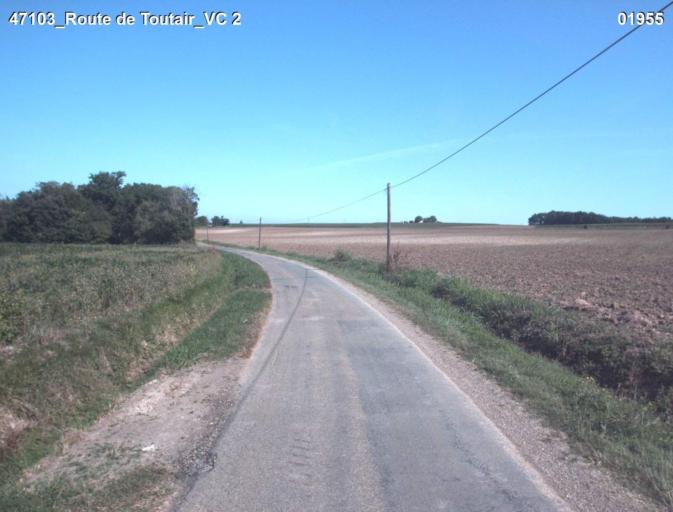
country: FR
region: Aquitaine
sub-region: Departement du Lot-et-Garonne
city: Nerac
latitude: 44.0717
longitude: 0.3337
